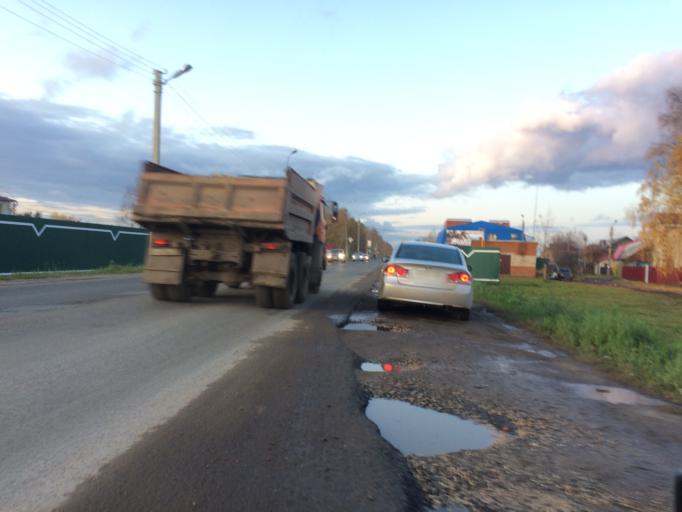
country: RU
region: Mariy-El
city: Yoshkar-Ola
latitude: 56.6525
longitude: 47.8992
